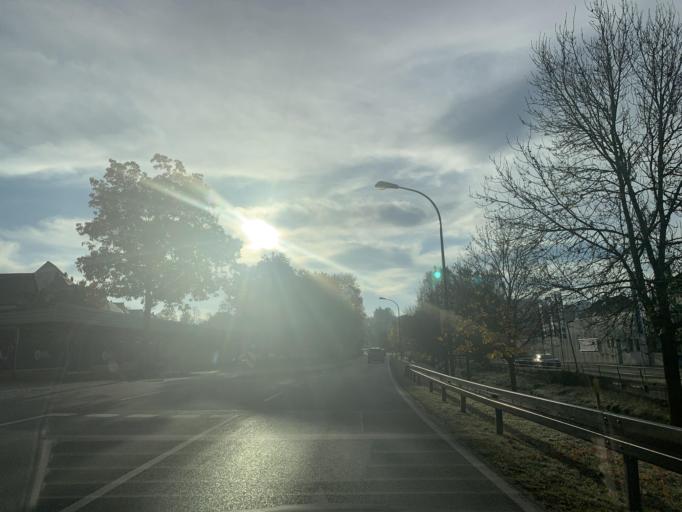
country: DE
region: Bavaria
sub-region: Upper Palatinate
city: Neunburg vorm Wald
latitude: 49.3477
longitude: 12.3841
